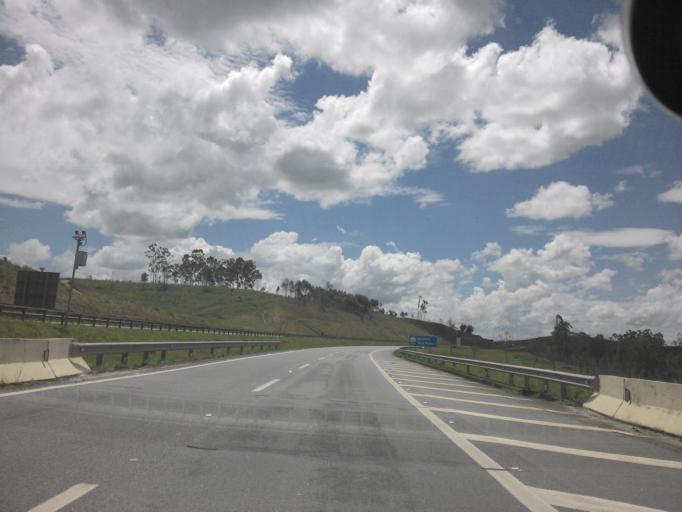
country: BR
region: Sao Paulo
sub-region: Jacarei
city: Jacarei
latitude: -23.3379
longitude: -46.0241
